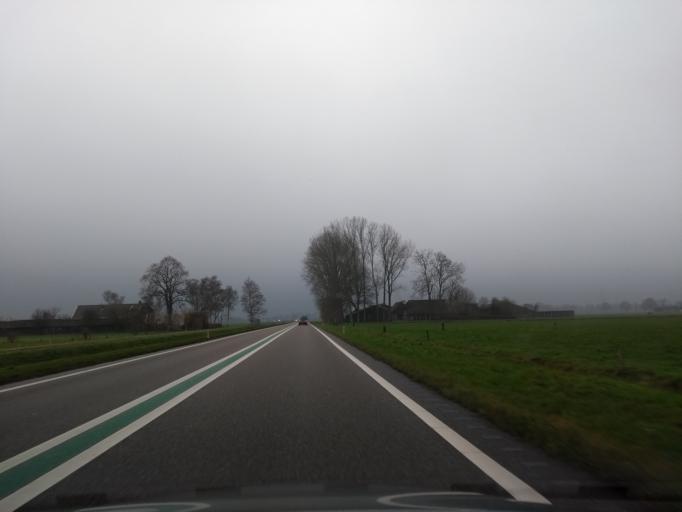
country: NL
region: Overijssel
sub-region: Gemeente Twenterand
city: Den Ham
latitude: 52.5879
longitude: 6.4114
